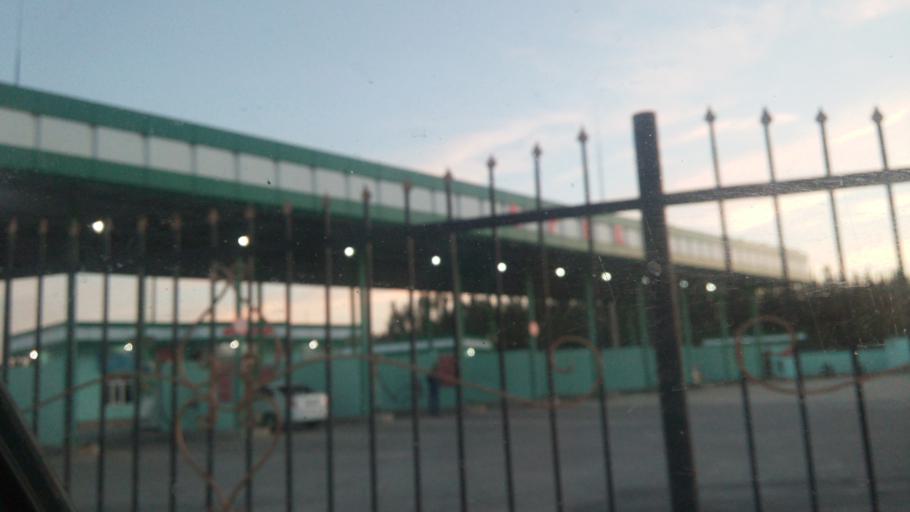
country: UZ
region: Navoiy
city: Yangirabot
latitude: 39.9356
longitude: 66.0782
